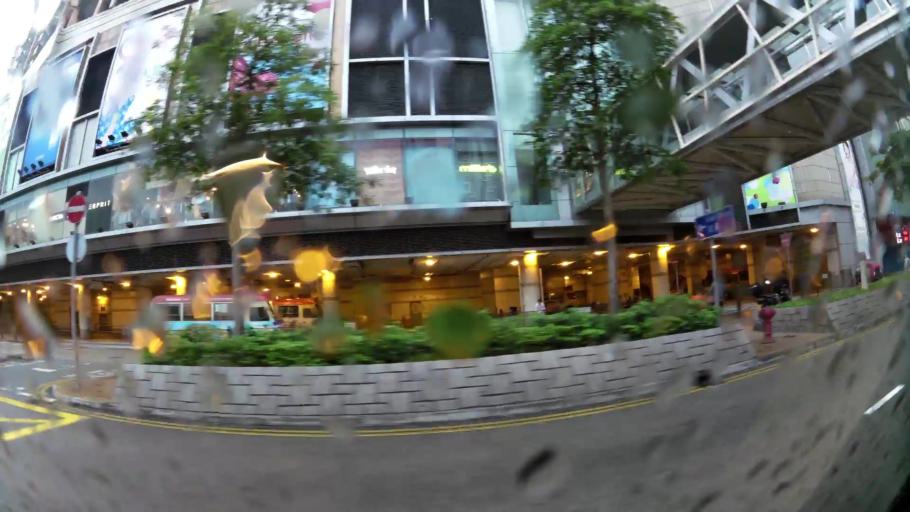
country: HK
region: Tsuen Wan
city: Tsuen Wan
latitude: 22.3702
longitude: 114.1133
